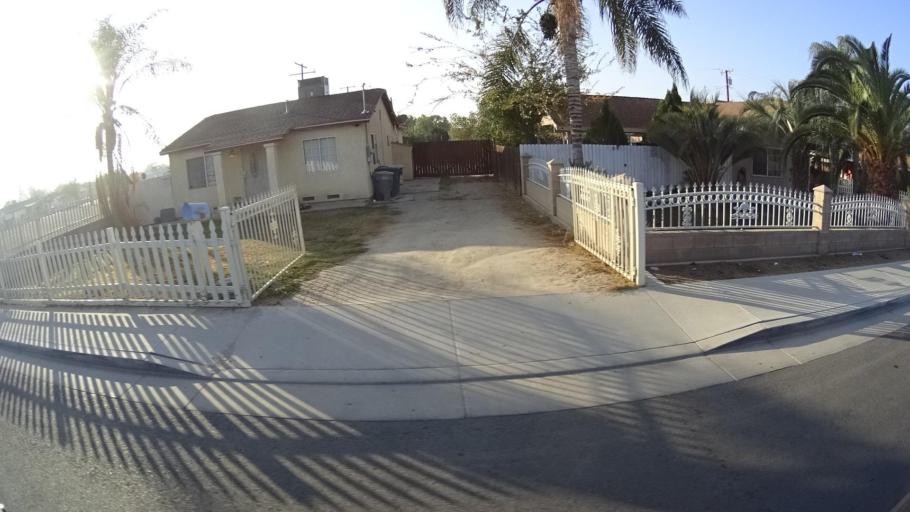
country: US
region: California
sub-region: Kern County
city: Delano
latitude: 35.7904
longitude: -119.2396
